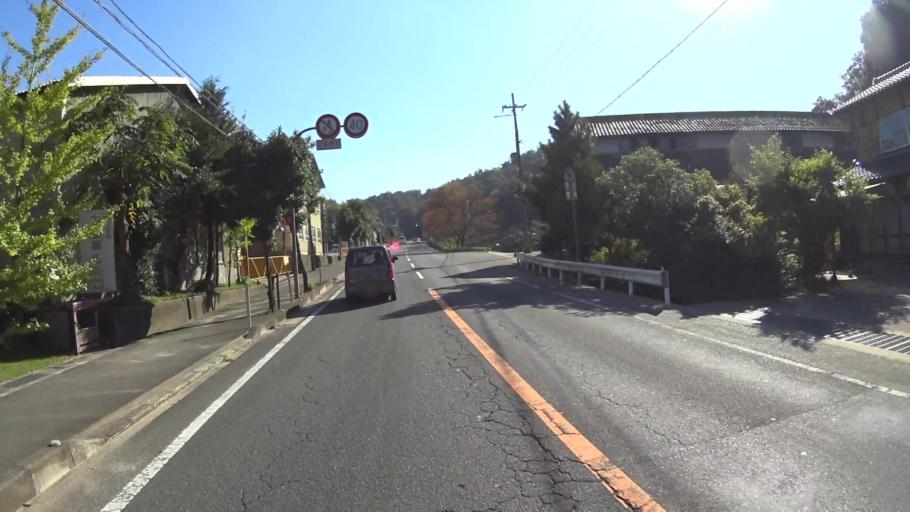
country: JP
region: Kyoto
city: Miyazu
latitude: 35.6382
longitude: 135.0547
